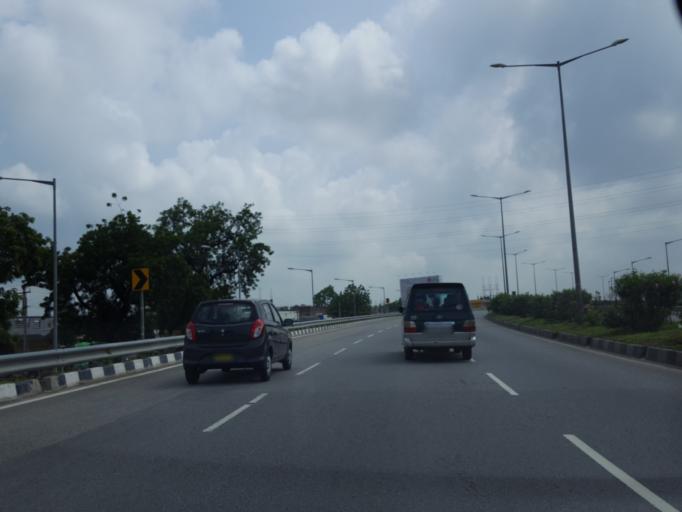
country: IN
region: Telangana
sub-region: Nalgonda
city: Bhongir
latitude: 17.2329
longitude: 78.9828
